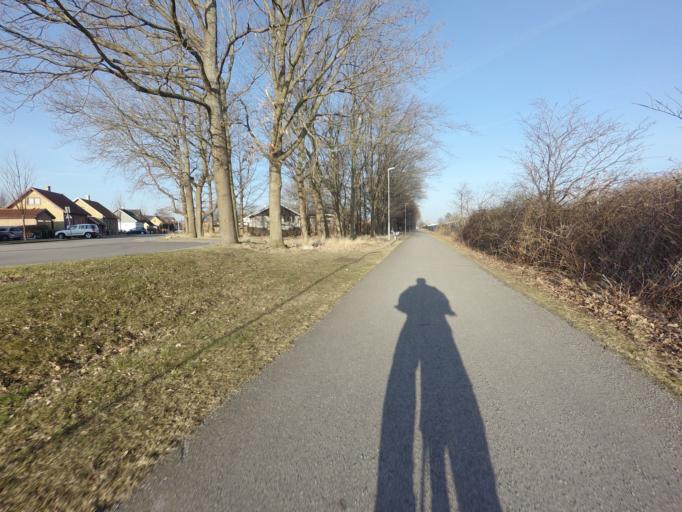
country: SE
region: Skane
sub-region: Hoganas Kommun
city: Hoganas
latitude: 56.2005
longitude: 12.5819
